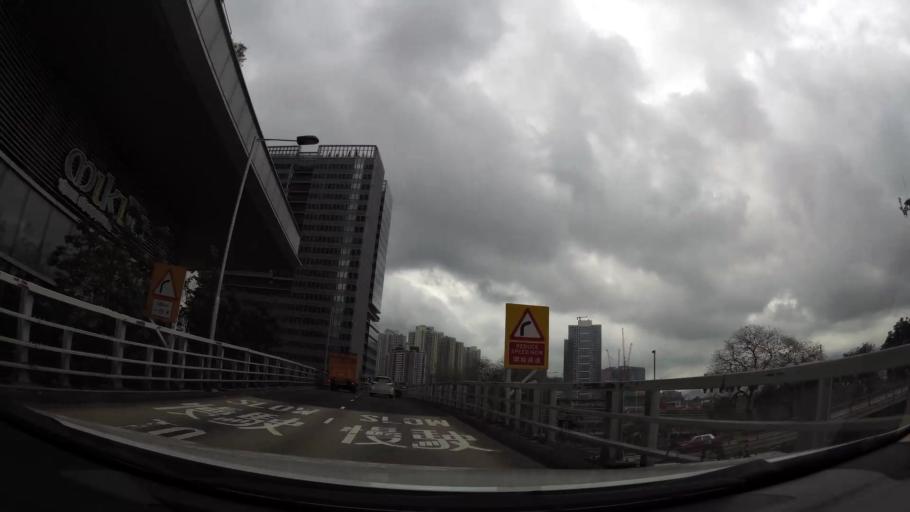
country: HK
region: Kowloon City
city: Kowloon
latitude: 22.3331
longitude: 114.1958
